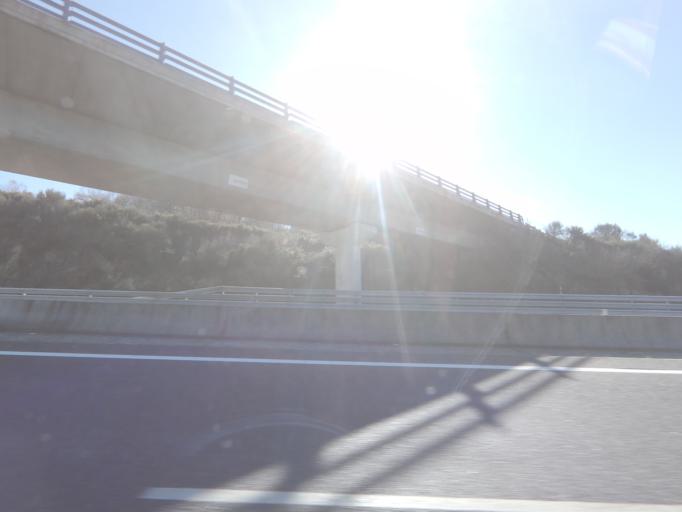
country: ES
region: Galicia
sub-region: Provincia de Pontevedra
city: Dozon
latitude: 42.5659
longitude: -8.0509
